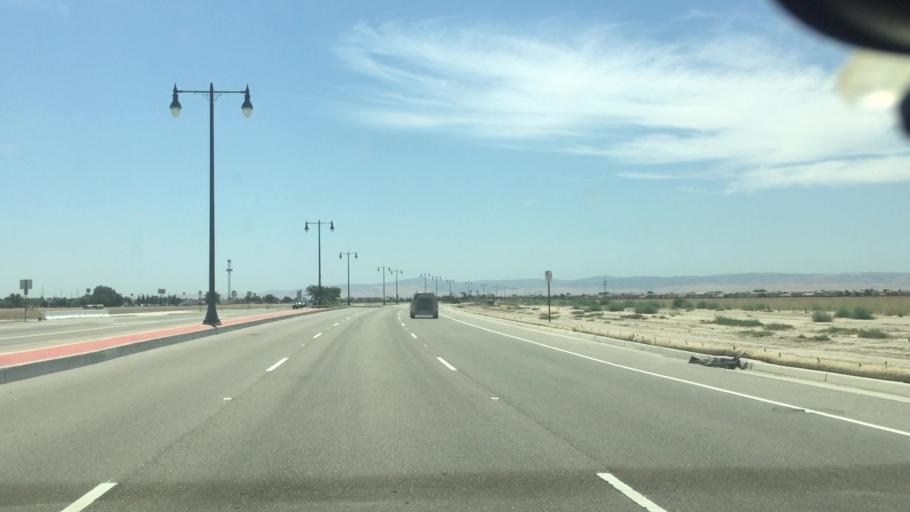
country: US
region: California
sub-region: San Joaquin County
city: Lathrop
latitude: 37.8255
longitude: -121.2957
